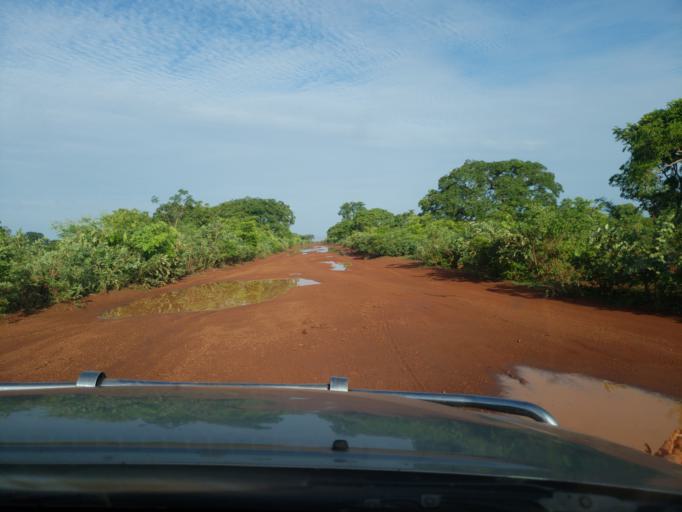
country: ML
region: Sikasso
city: Koutiala
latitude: 12.4270
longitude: -5.6362
